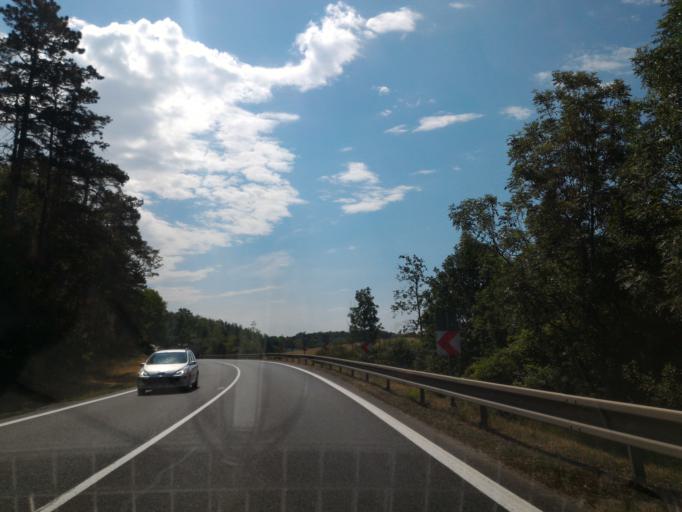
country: CZ
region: South Moravian
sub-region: Okres Znojmo
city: Jevisovice
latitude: 48.9145
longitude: 15.9612
